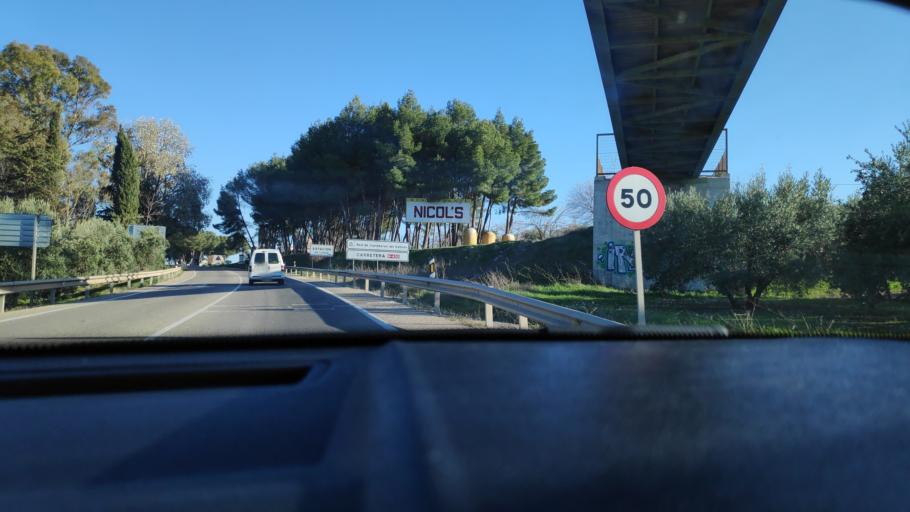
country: ES
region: Andalusia
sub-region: Province of Cordoba
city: Luque
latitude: 37.5738
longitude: -4.2650
